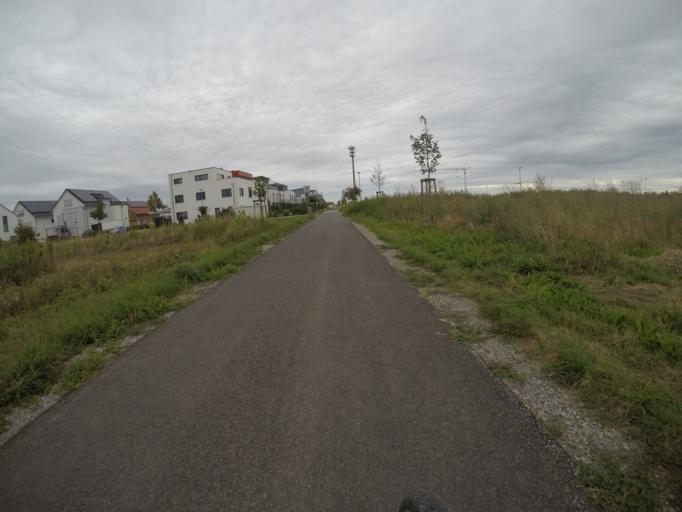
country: DE
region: Baden-Wuerttemberg
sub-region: Regierungsbezirk Stuttgart
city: Holzgerlingen
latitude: 48.6410
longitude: 9.0024
